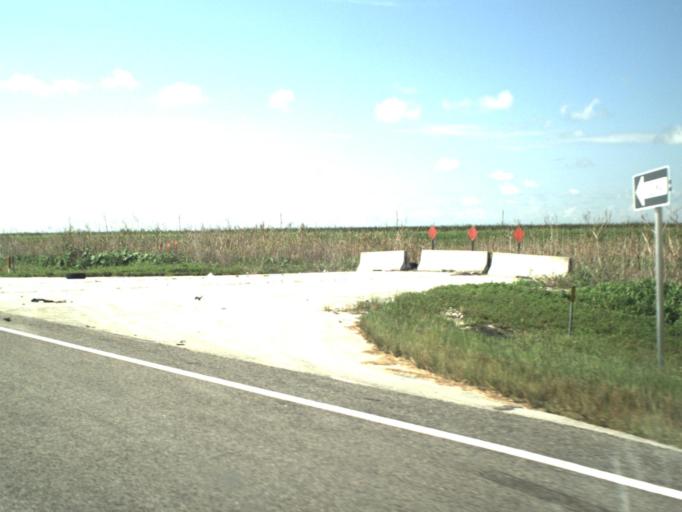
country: US
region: Florida
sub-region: Broward County
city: Coral Springs
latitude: 26.3699
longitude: -80.5651
